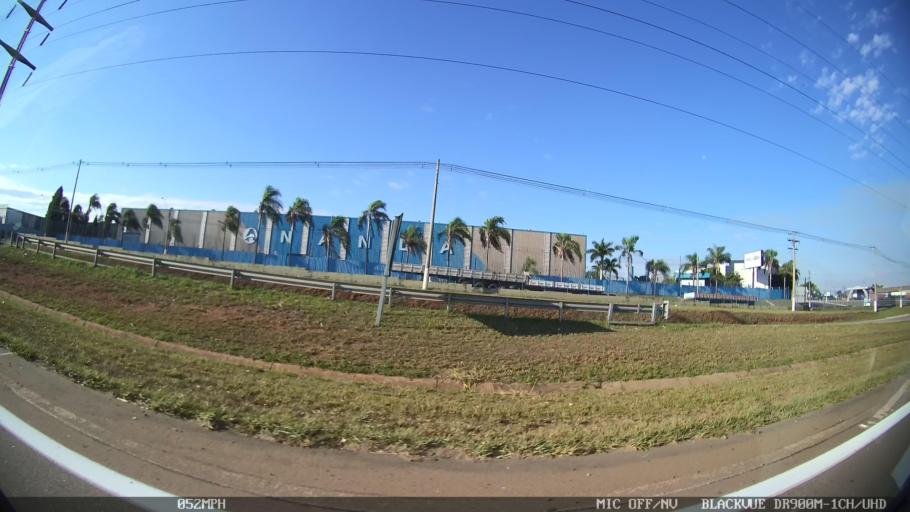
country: BR
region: Sao Paulo
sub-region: Piracicaba
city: Piracicaba
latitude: -22.6633
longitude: -47.6088
